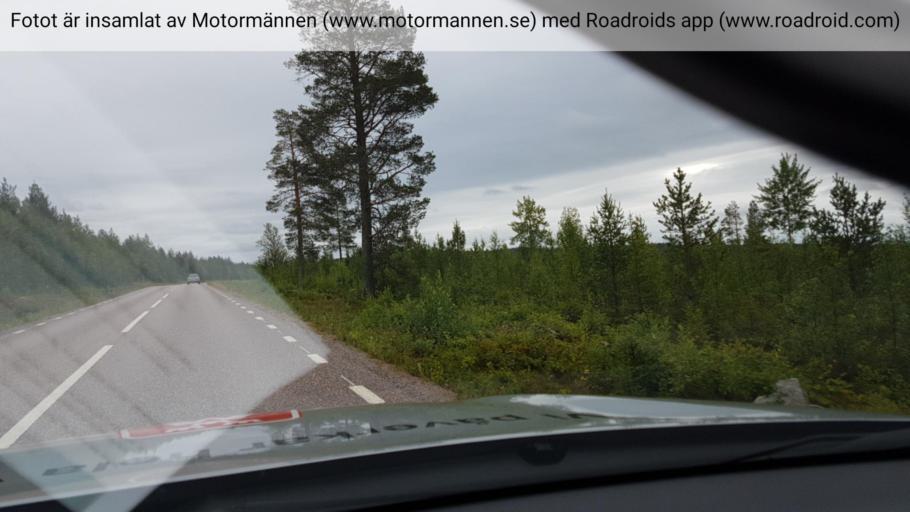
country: SE
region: Norrbotten
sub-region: Gallivare Kommun
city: Gaellivare
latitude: 67.0441
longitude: 21.6346
